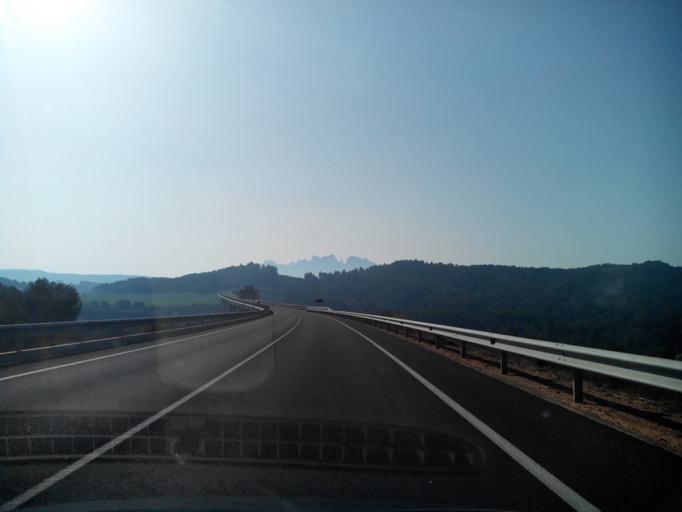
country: ES
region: Catalonia
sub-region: Provincia de Barcelona
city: Sant Joan de Vilatorrada
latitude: 41.7232
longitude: 1.7814
